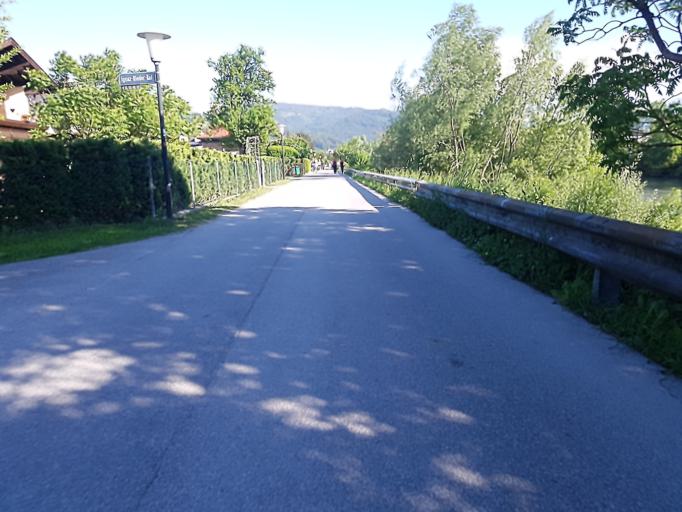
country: AT
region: Salzburg
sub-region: Salzburg Stadt
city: Salzburg
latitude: 47.7891
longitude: 13.0710
